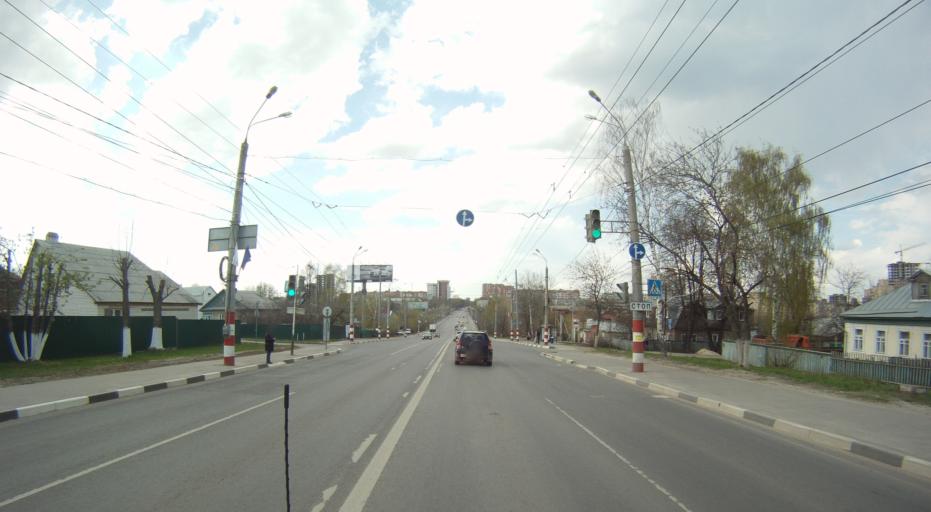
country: RU
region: Nizjnij Novgorod
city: Nizhniy Novgorod
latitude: 56.3032
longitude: 44.0288
